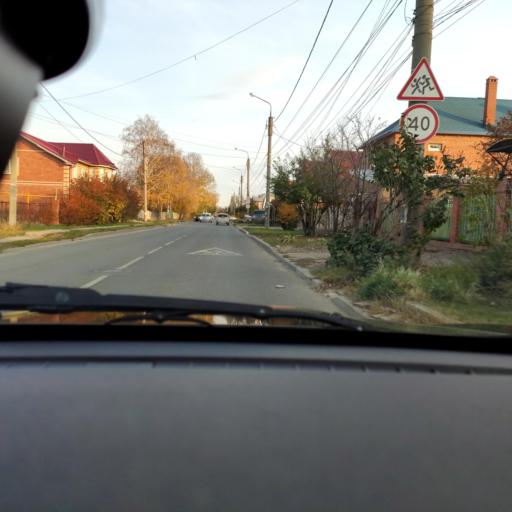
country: RU
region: Samara
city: Tol'yatti
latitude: 53.5269
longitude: 49.4207
